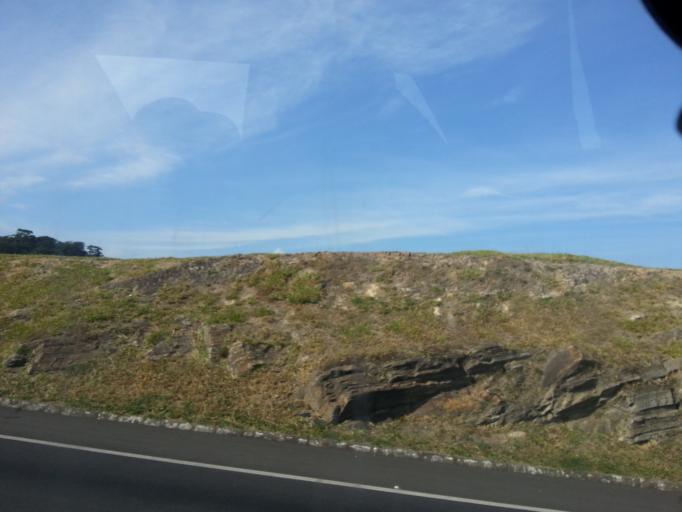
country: BR
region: Rio de Janeiro
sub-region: Volta Redonda
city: Volta Redonda
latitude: -22.5879
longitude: -44.0925
